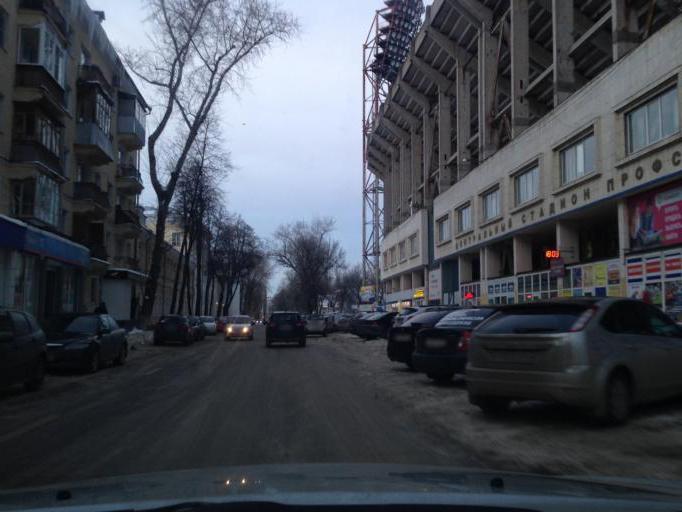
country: RU
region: Voronezj
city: Voronezh
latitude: 51.6728
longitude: 39.2025
